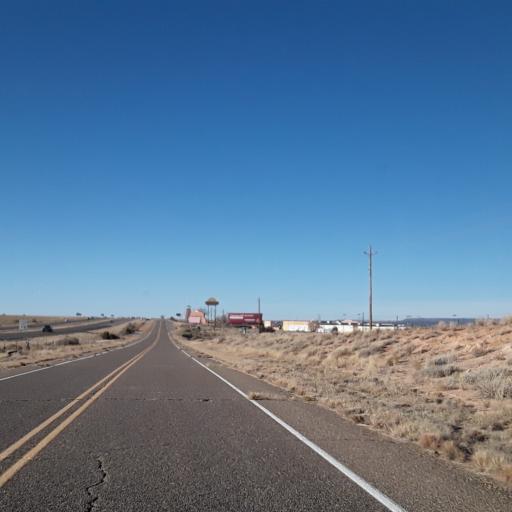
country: US
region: New Mexico
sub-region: Sandoval County
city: Santo Domingo Pueblo
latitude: 35.4558
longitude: -106.3407
